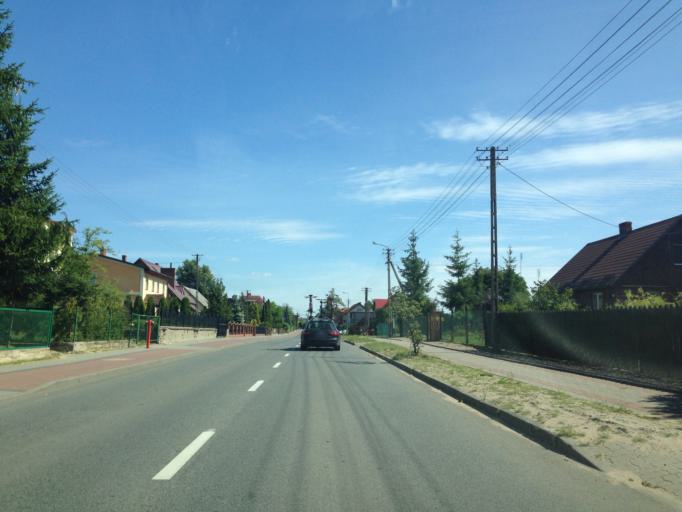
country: PL
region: Kujawsko-Pomorskie
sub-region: Powiat swiecki
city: Osie
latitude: 53.6019
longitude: 18.3376
